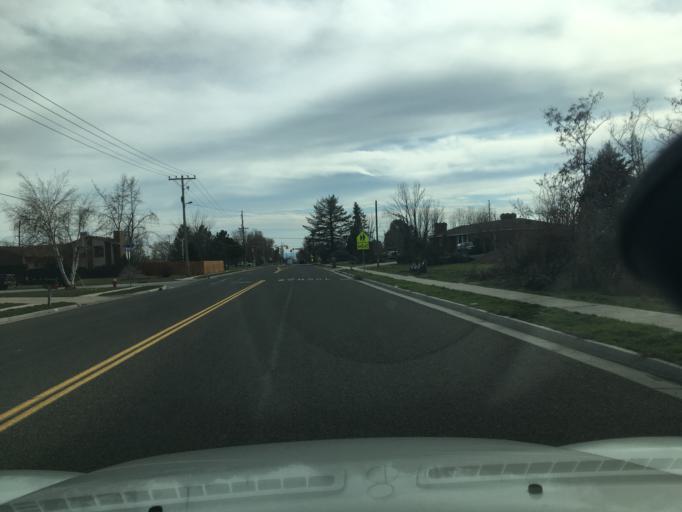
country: US
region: Utah
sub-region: Davis County
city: Clearfield
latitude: 41.0765
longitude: -112.0070
